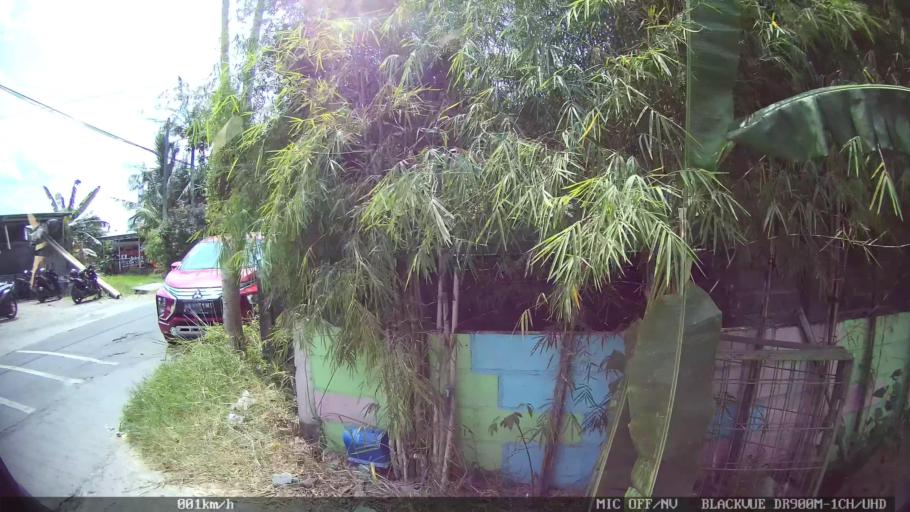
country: ID
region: Daerah Istimewa Yogyakarta
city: Kasihan
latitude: -7.8165
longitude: 110.3433
